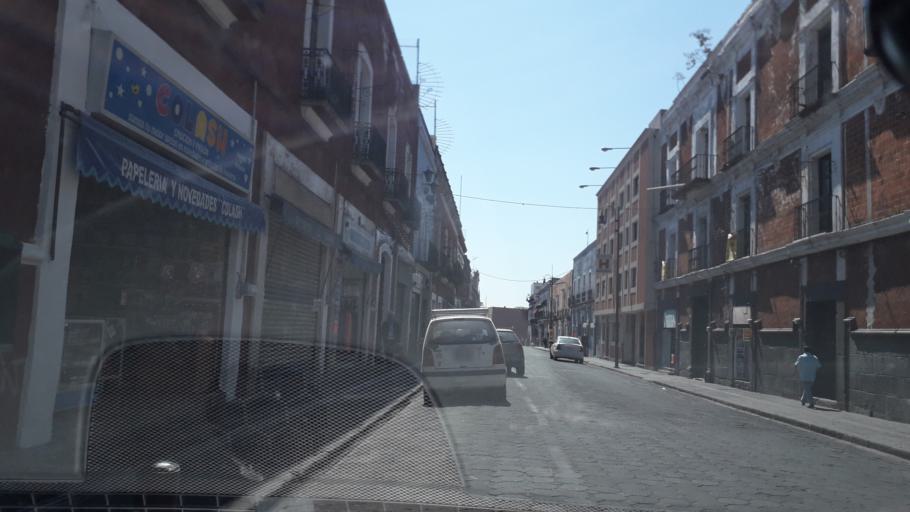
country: MX
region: Puebla
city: Puebla
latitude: 19.0459
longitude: -98.1938
